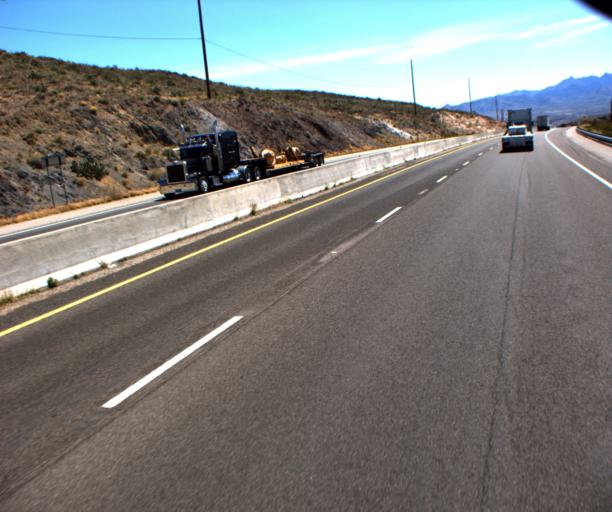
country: US
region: Arizona
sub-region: Mohave County
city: Kingman
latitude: 35.2081
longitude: -114.1008
